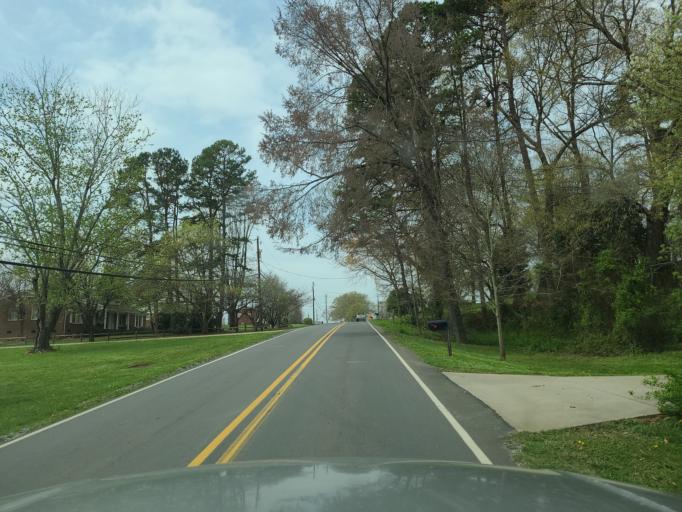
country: US
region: North Carolina
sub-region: Cleveland County
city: Shelby
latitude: 35.3287
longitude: -81.5061
